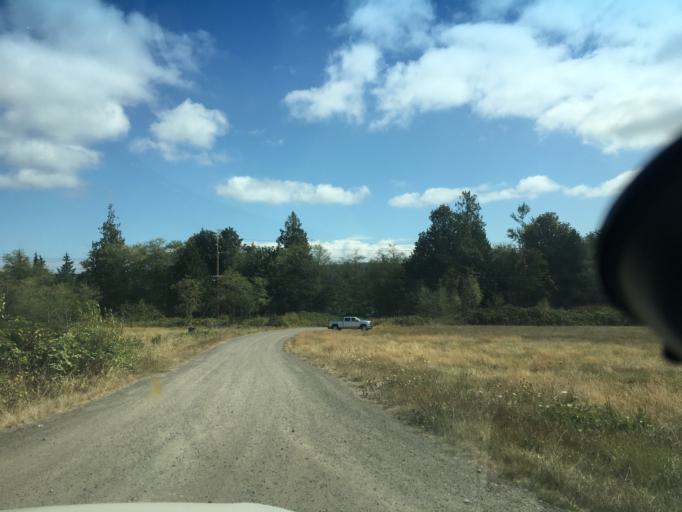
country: US
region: Washington
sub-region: Kitsap County
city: Hansville
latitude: 47.8477
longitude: -122.5872
